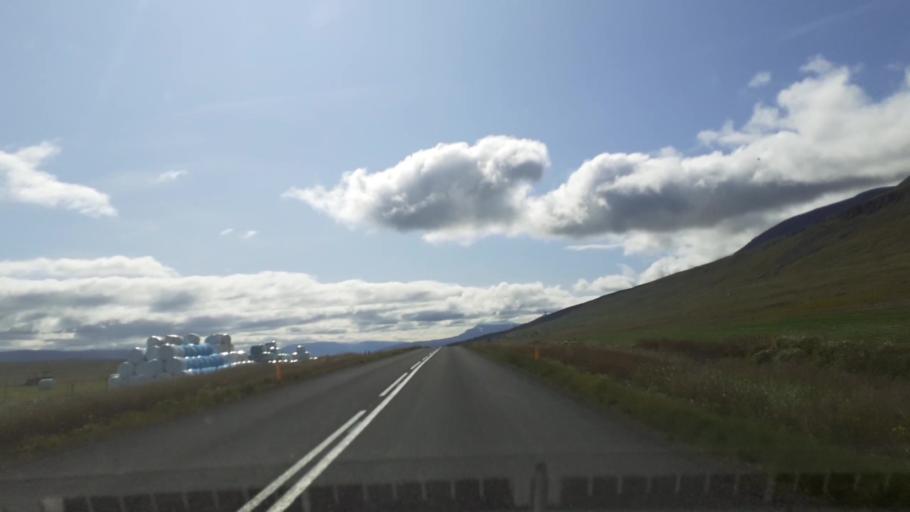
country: IS
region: Northeast
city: Akureyri
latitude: 65.8572
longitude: -18.2592
